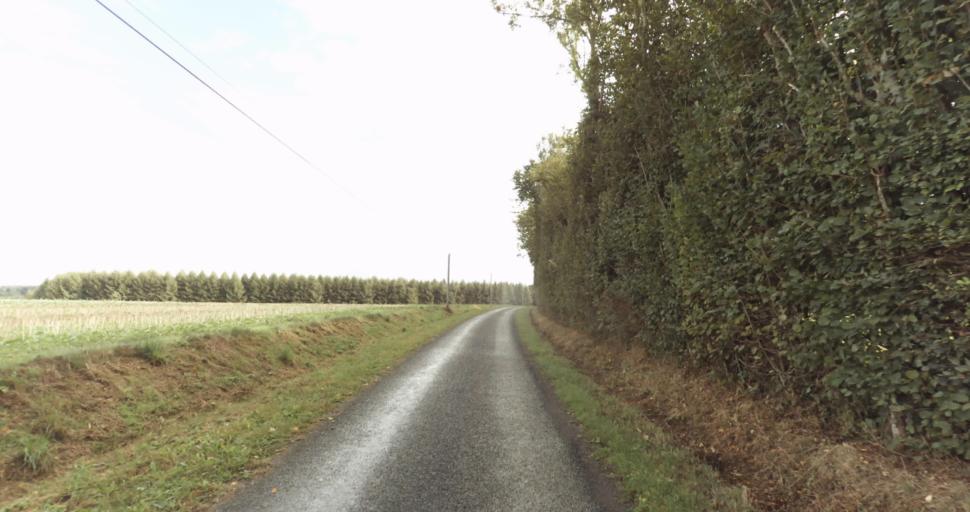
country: FR
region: Lower Normandy
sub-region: Departement de l'Orne
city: Sainte-Gauburge-Sainte-Colombe
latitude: 48.6859
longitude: 0.3755
